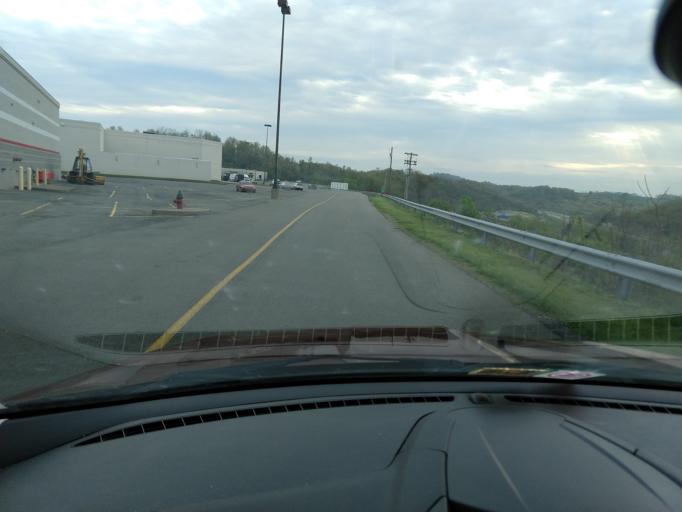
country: US
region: West Virginia
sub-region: Harrison County
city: Bridgeport
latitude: 39.3108
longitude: -80.2736
